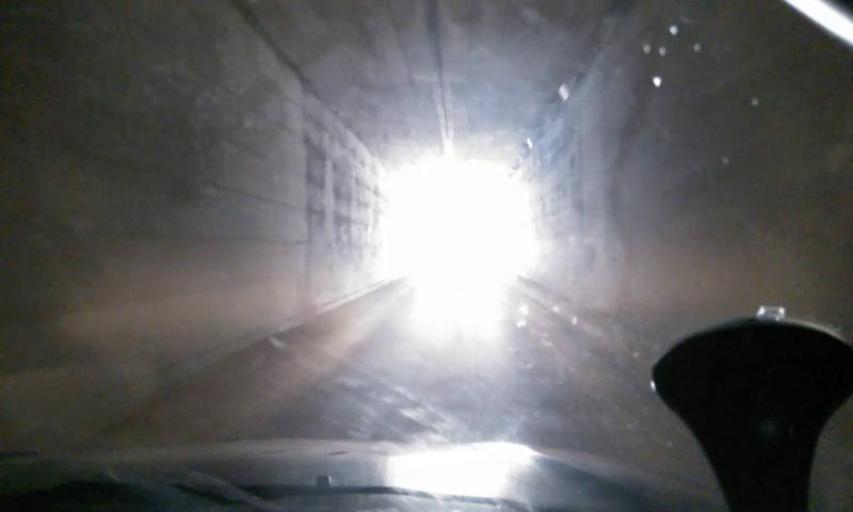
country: IL
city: Giv'on HaHadasha
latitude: 31.8418
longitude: 35.1707
